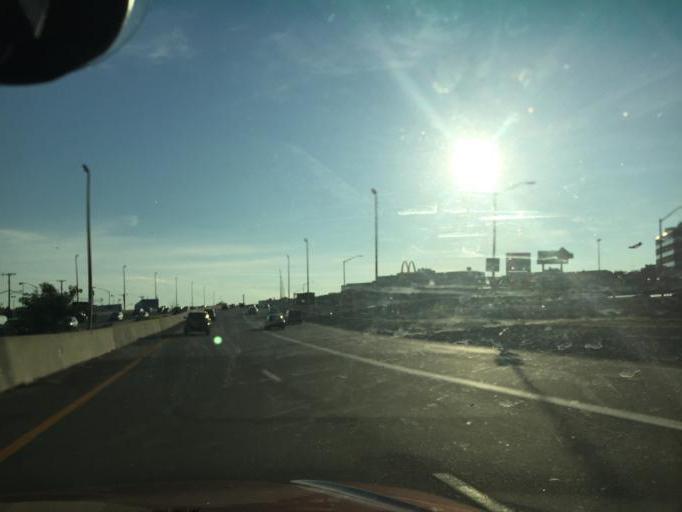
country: US
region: New York
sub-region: Queens County
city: Jamaica
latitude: 40.7696
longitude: -73.8360
